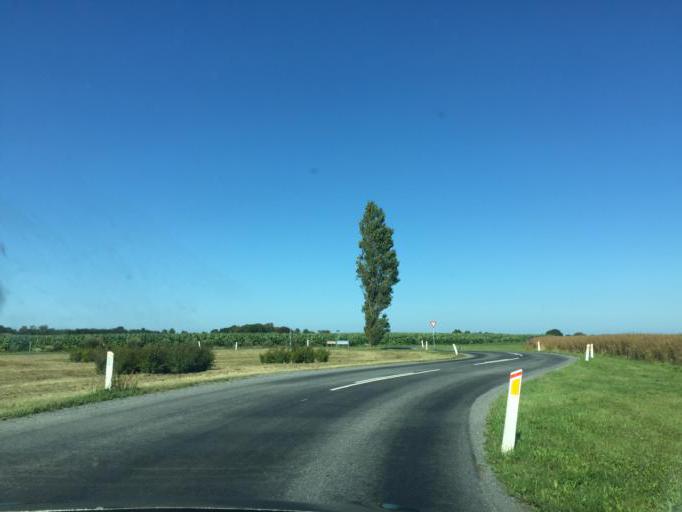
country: DK
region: South Denmark
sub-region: Nordfyns Kommune
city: Sonderso
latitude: 55.4912
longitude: 10.2865
